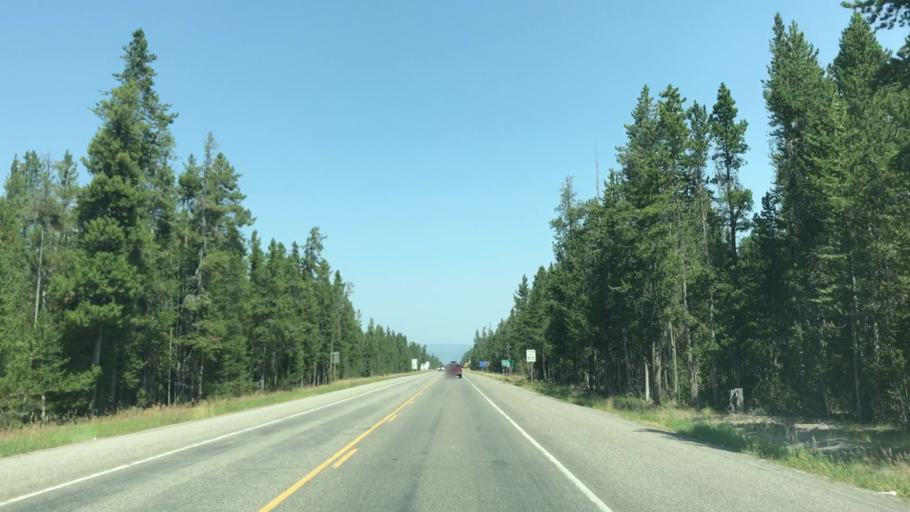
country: US
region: Montana
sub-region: Gallatin County
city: West Yellowstone
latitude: 44.6684
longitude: -111.1000
